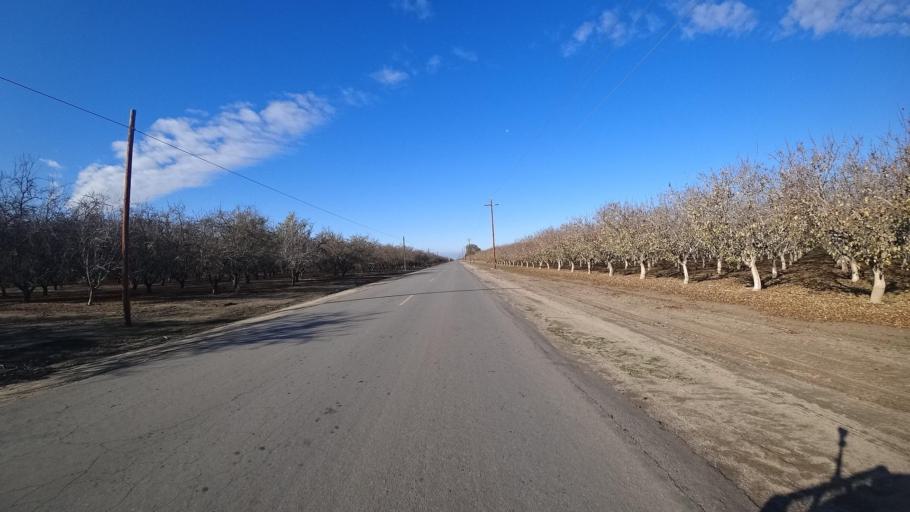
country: US
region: California
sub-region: Kern County
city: McFarland
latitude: 35.6887
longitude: -119.2958
